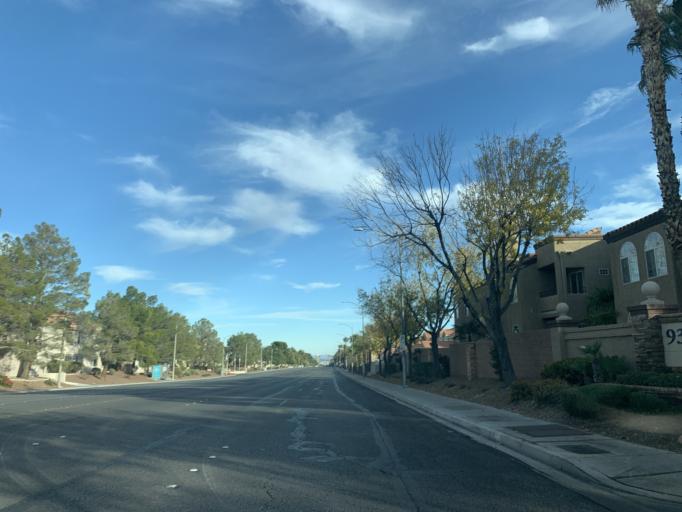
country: US
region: Nevada
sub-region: Clark County
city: Summerlin South
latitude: 36.1297
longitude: -115.2944
